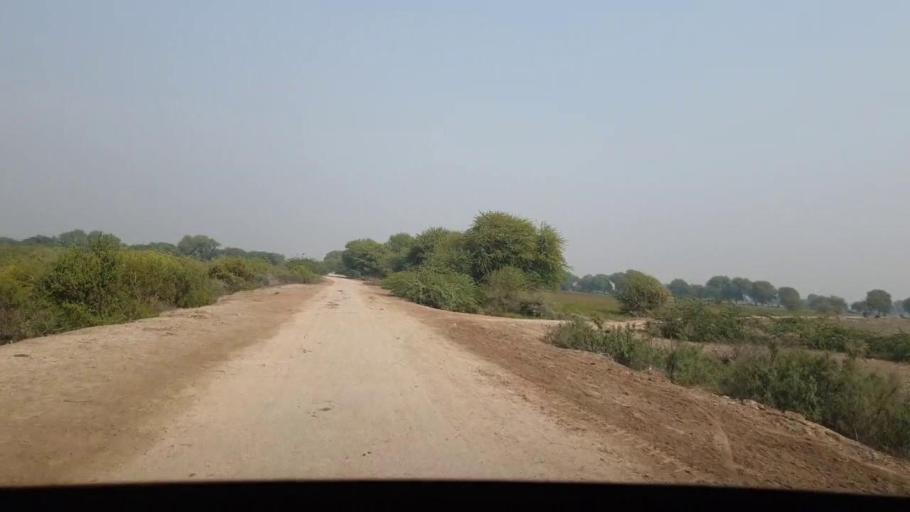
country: PK
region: Sindh
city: Jati
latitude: 24.4319
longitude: 68.4342
